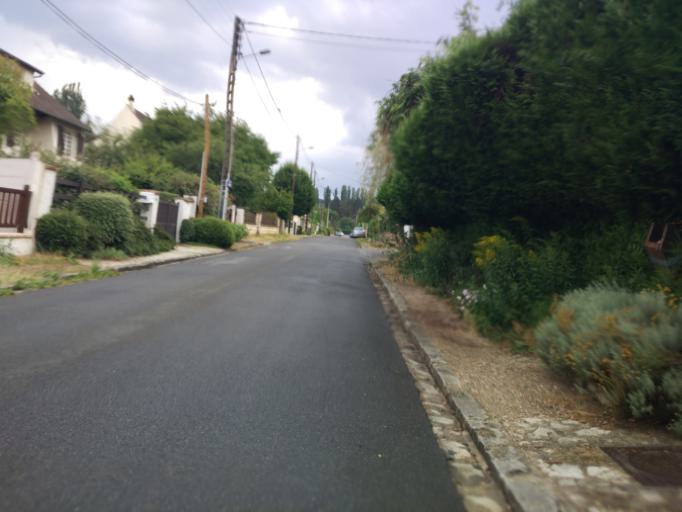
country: FR
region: Ile-de-France
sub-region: Departement des Yvelines
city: Saint-Remy-les-Chevreuse
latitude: 48.6983
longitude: 2.0644
